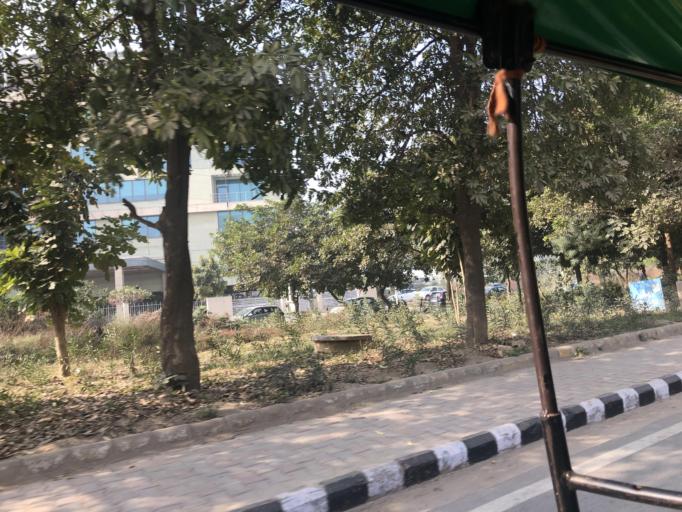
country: IN
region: Haryana
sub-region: Gurgaon
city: Gurgaon
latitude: 28.4500
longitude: 77.0772
